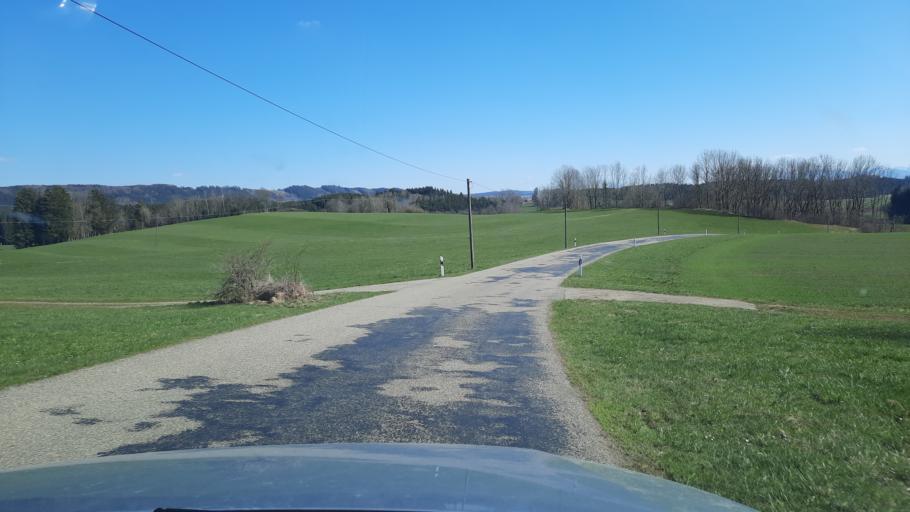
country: DE
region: Bavaria
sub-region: Swabia
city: Wolfertschwenden
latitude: 47.8574
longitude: 10.2464
